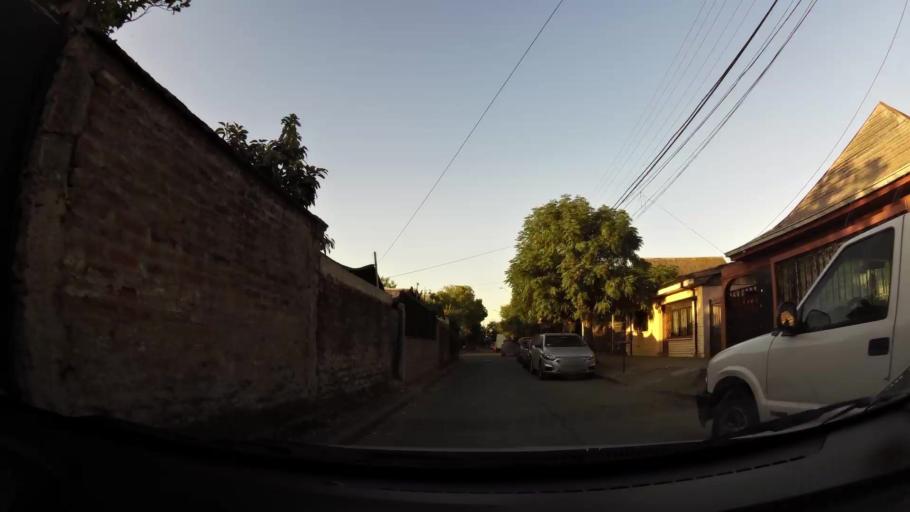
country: CL
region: Maule
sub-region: Provincia de Talca
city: Talca
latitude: -35.4480
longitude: -71.6673
